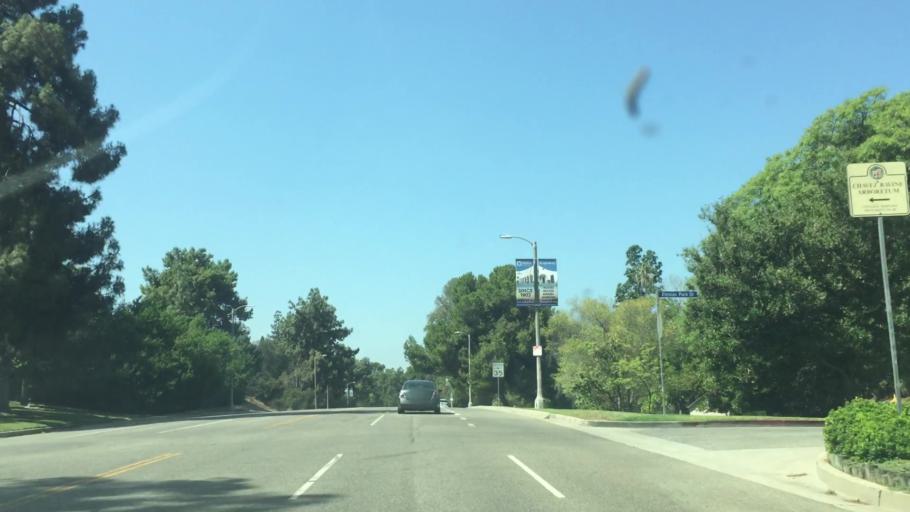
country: US
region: California
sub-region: Los Angeles County
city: Echo Park
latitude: 34.0862
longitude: -118.2431
